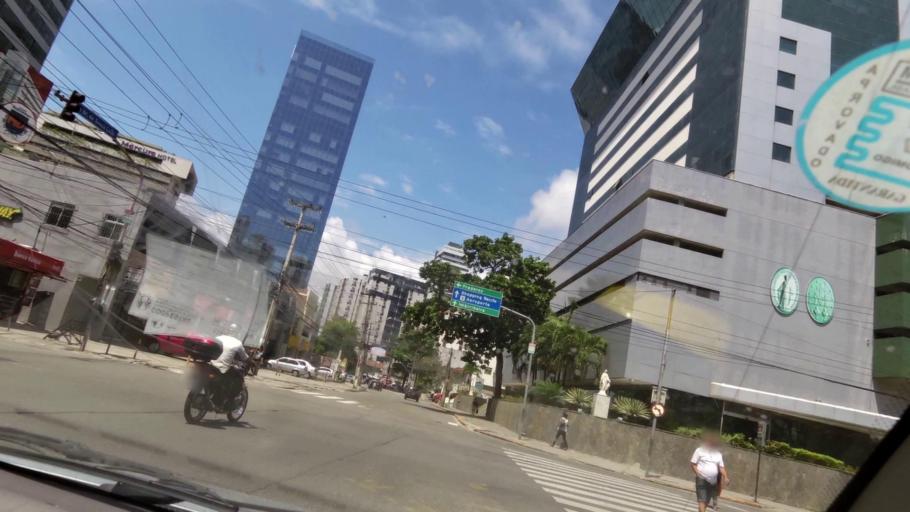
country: BR
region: Espirito Santo
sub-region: Vila Velha
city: Vila Velha
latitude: -20.3200
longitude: -40.3049
